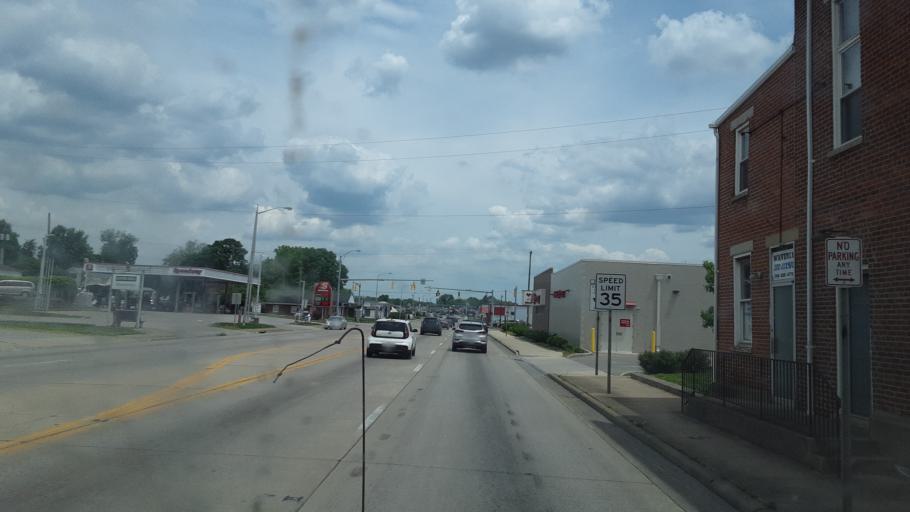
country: US
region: Ohio
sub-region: Pike County
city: Waverly
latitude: 39.1275
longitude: -82.9836
